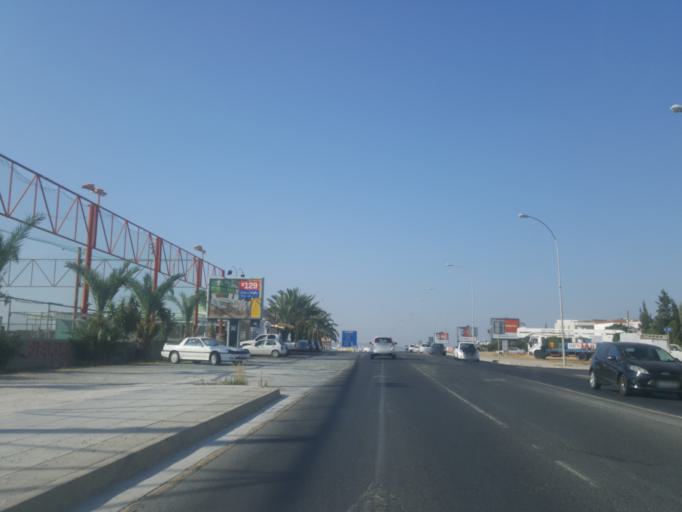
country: CY
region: Lefkosia
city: Nicosia
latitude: 35.1312
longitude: 33.3574
